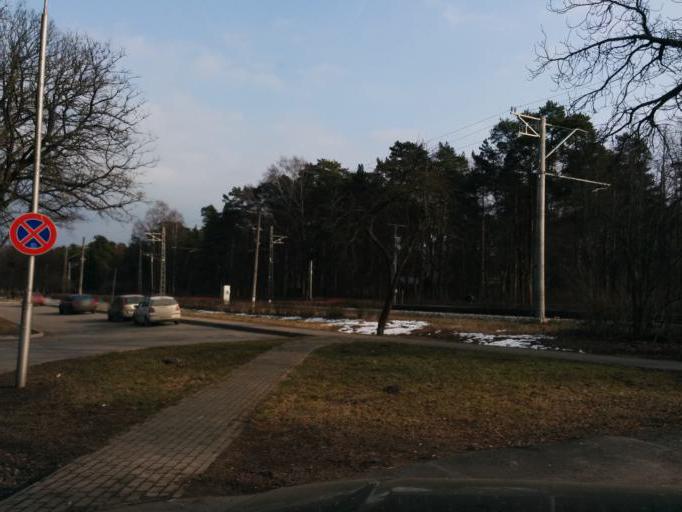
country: LV
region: Jurmala
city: Jurmala
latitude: 56.9721
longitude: 23.8141
